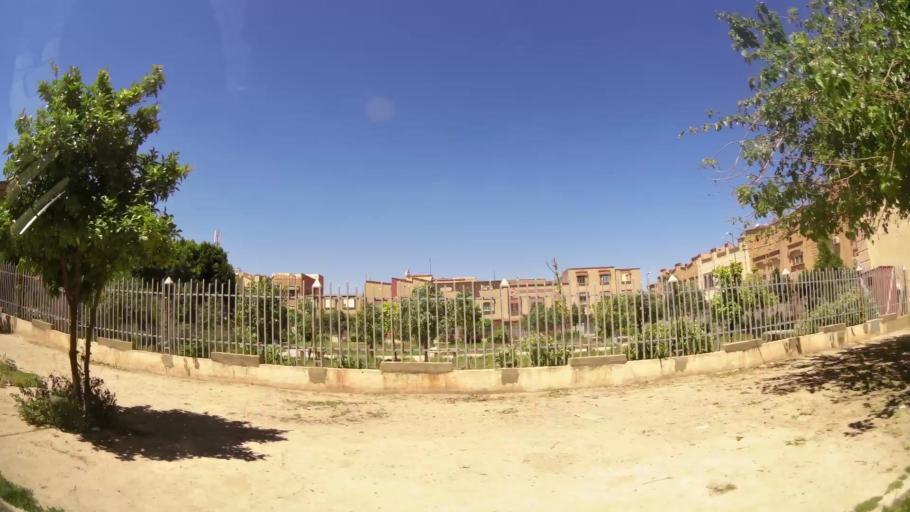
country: MA
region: Oriental
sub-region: Oujda-Angad
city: Oujda
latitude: 34.6687
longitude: -1.8864
